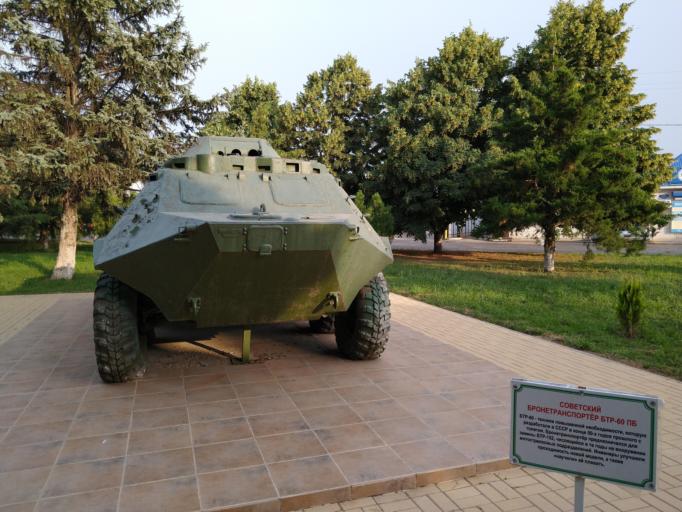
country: RU
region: Krasnodarskiy
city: Kavkazskaya
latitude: 45.4360
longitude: 40.6505
